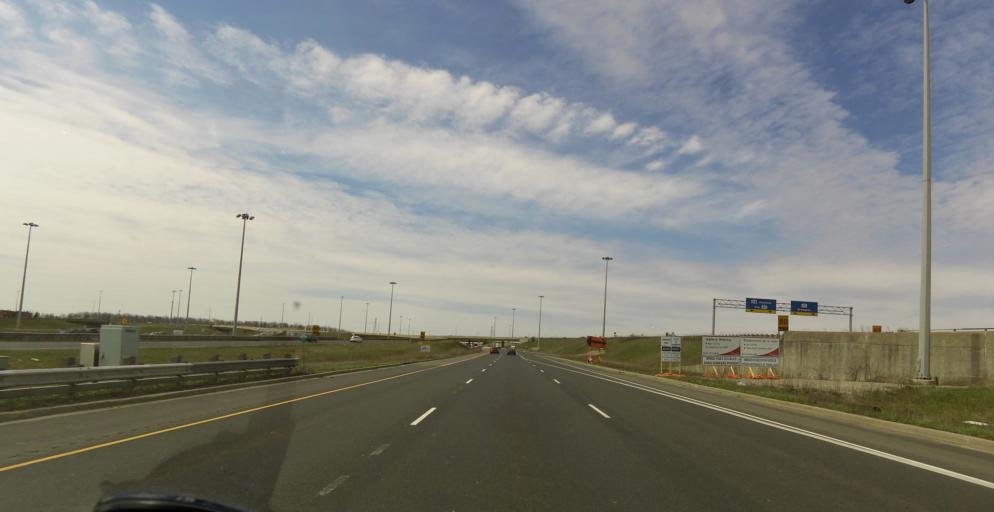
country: CA
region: Ontario
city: Mississauga
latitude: 43.6446
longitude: -79.6490
